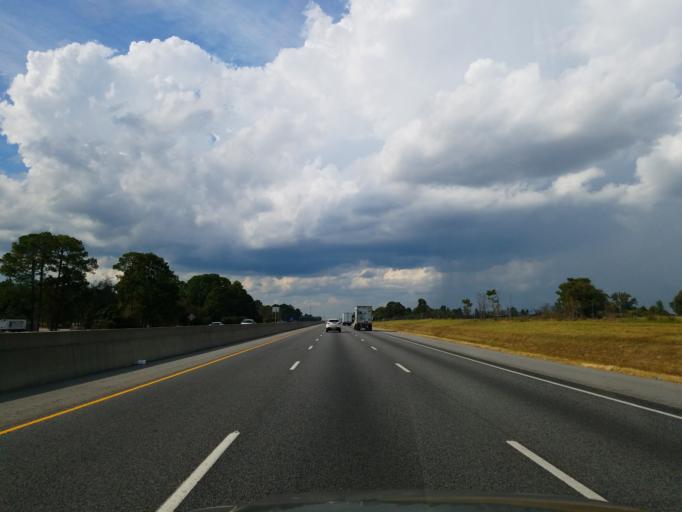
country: US
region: Georgia
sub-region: Turner County
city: Ashburn
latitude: 31.6333
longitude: -83.5817
